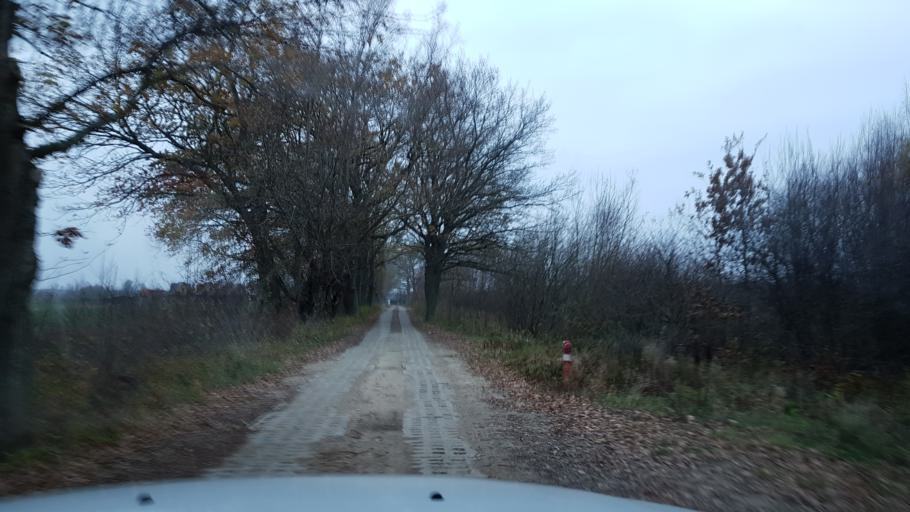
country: PL
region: West Pomeranian Voivodeship
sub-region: Powiat slawienski
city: Darlowo
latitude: 54.5100
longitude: 16.4891
